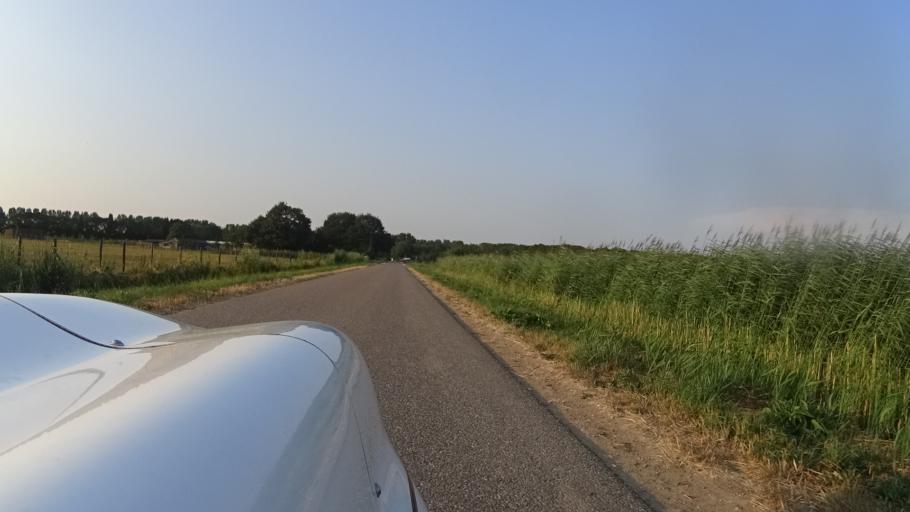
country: NL
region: Gelderland
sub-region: Gemeente Buren
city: Lienden
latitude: 51.9059
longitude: 5.4855
